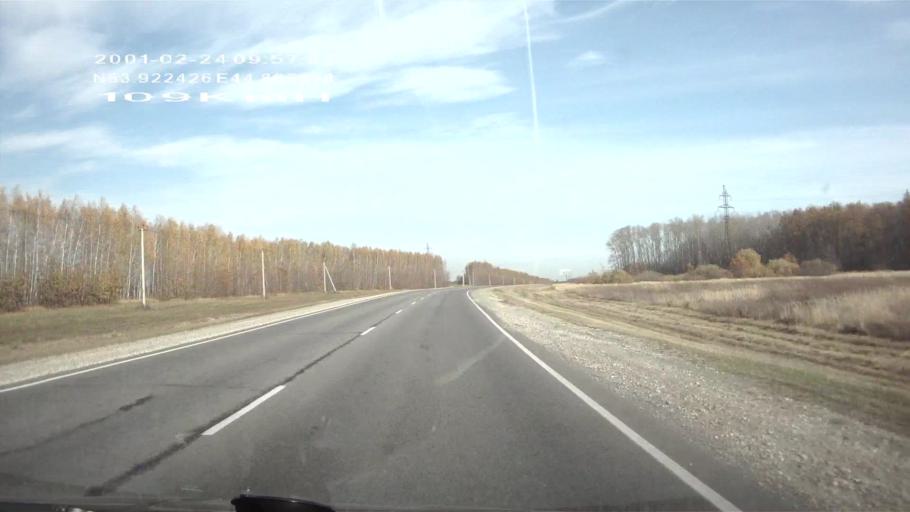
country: RU
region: Penza
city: Issa
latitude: 53.9229
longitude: 44.8652
